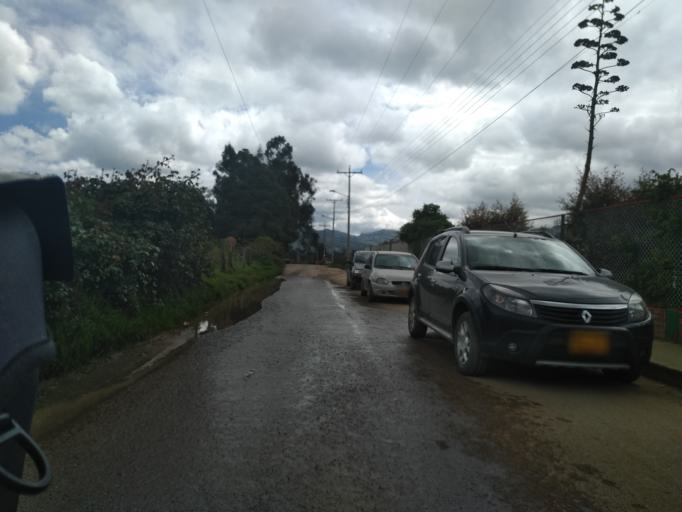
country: CO
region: Cundinamarca
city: Lenguazaque
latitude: 5.2993
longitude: -73.7128
